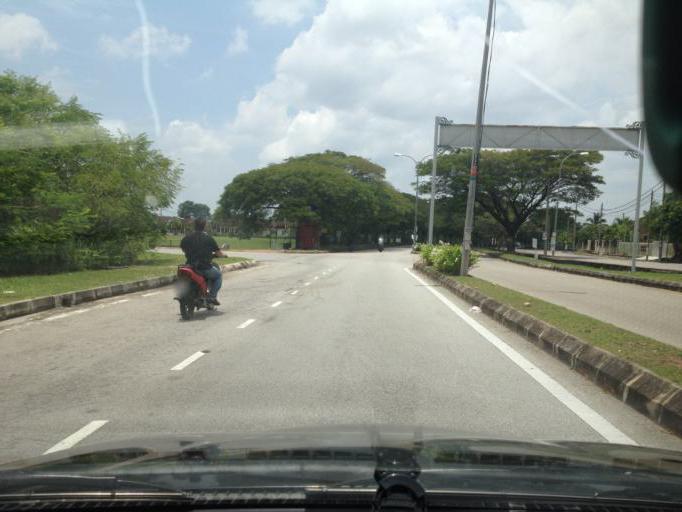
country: MY
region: Kedah
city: Sungai Petani
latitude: 5.6049
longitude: 100.5430
